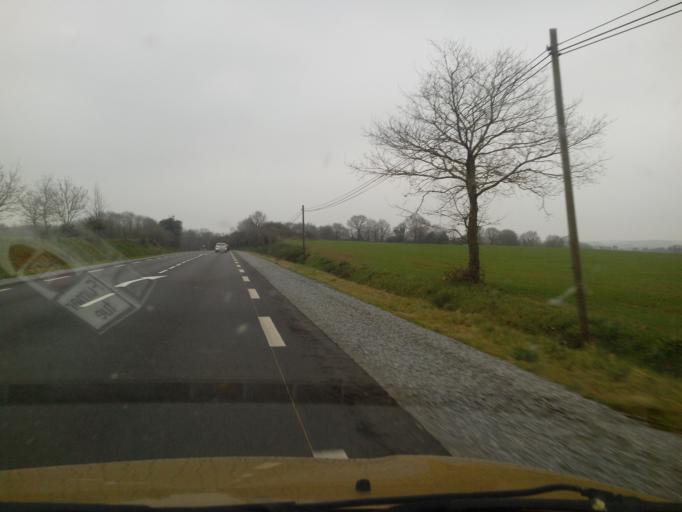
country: FR
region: Brittany
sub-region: Departement du Morbihan
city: Mauron
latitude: 48.0541
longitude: -2.2978
